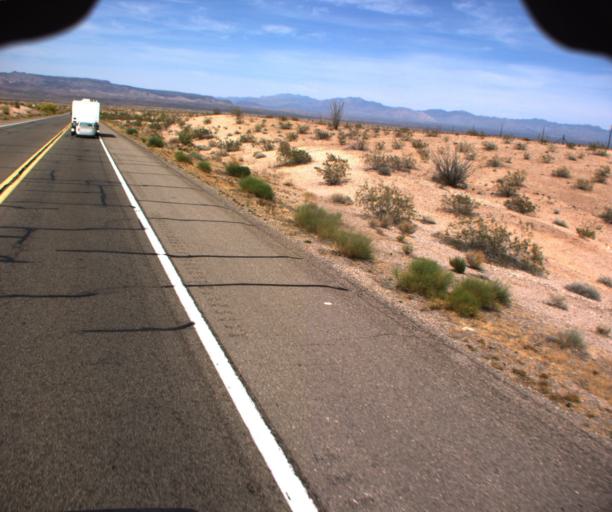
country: US
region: Arizona
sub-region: Mohave County
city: Desert Hills
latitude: 34.6705
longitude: -114.3106
